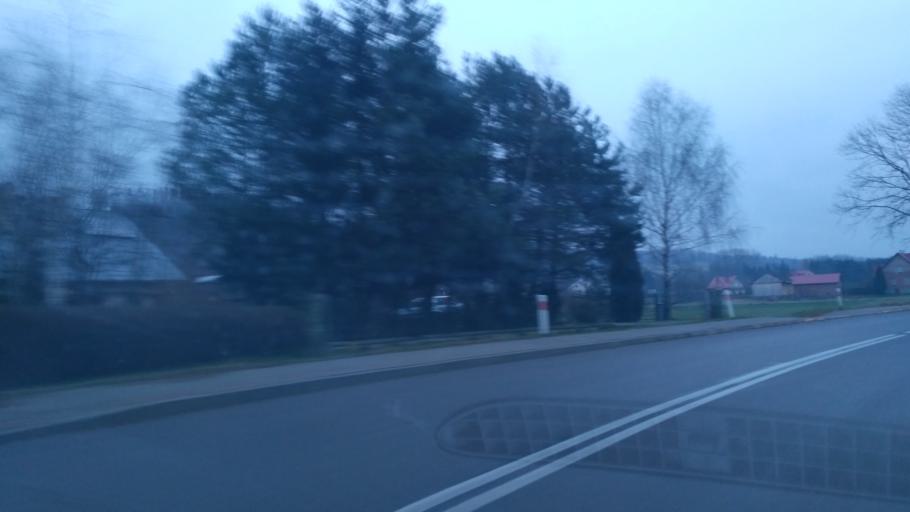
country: PL
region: Subcarpathian Voivodeship
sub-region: Powiat przemyski
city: Przedmiescie Dubieckie
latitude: 49.8306
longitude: 22.3633
